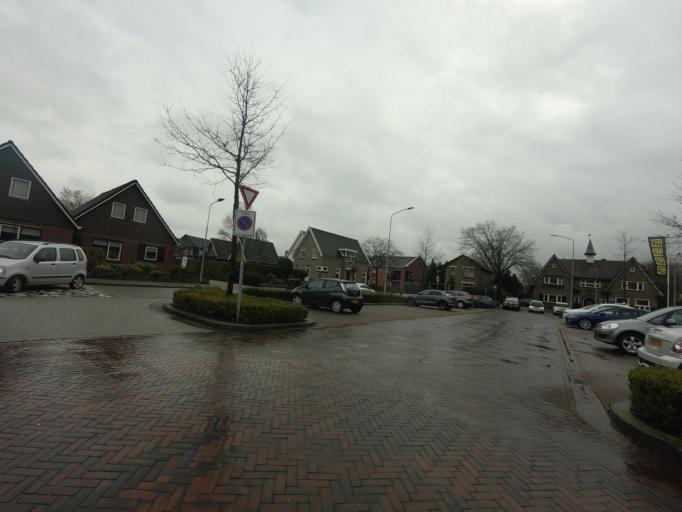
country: NL
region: Gelderland
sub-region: Gemeente Epe
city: Vaassen
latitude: 52.2877
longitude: 5.9703
